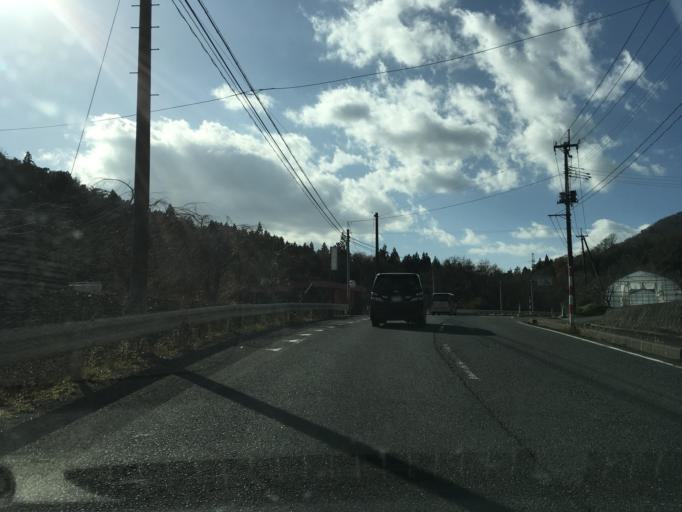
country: JP
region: Miyagi
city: Tomiya
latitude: 38.4300
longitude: 140.8634
